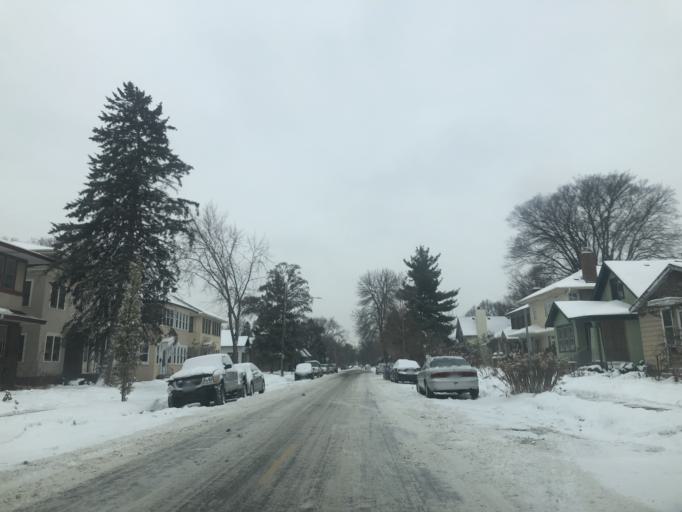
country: US
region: Minnesota
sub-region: Hennepin County
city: Richfield
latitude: 44.9280
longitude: -93.2844
